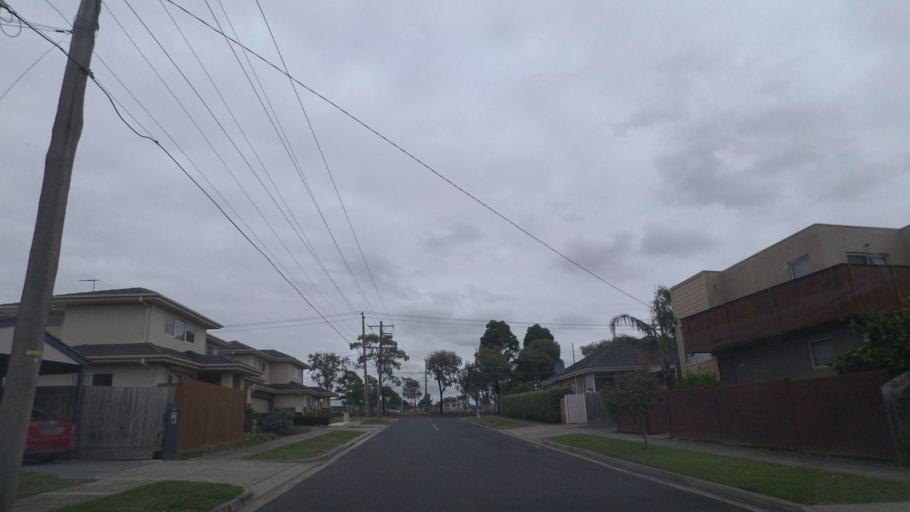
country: AU
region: Victoria
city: Forest Hill
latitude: -37.8354
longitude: 145.1837
